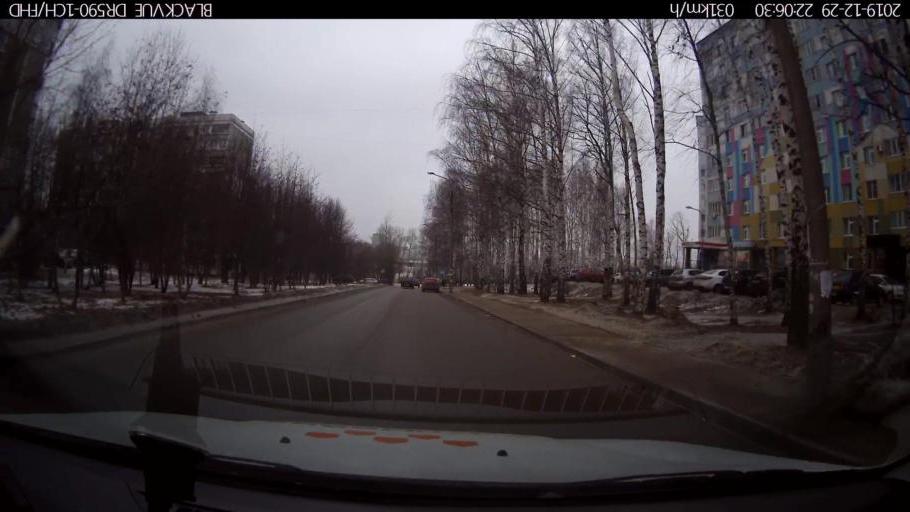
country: RU
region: Nizjnij Novgorod
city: Nizhniy Novgorod
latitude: 56.2236
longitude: 43.9515
